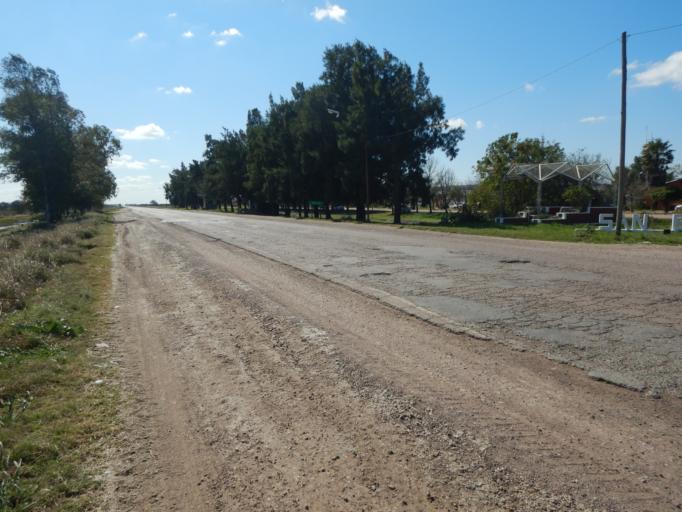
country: AR
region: Santa Fe
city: Tostado
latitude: -28.6691
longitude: -61.5303
